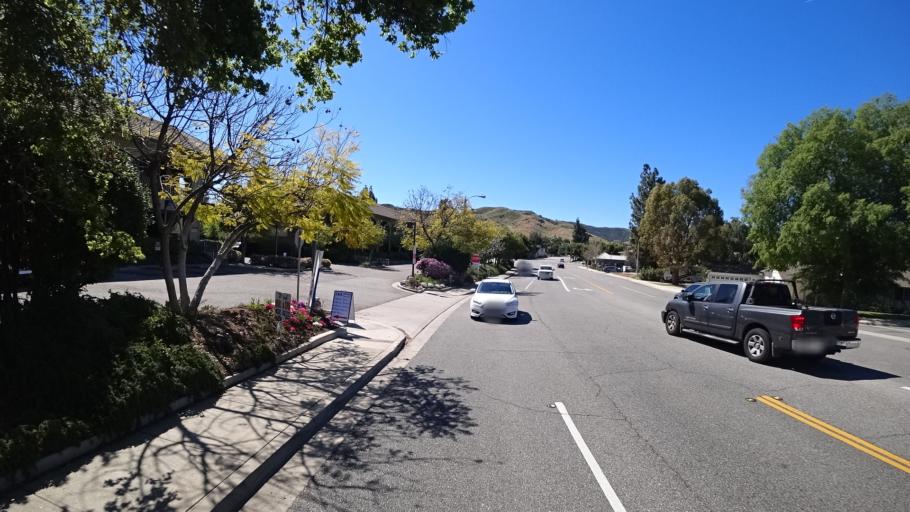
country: US
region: California
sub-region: Ventura County
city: Thousand Oaks
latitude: 34.1800
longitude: -118.8579
